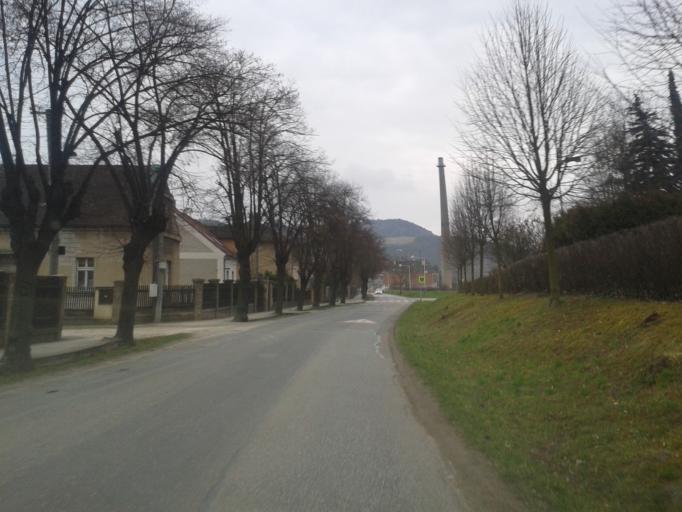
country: CZ
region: Central Bohemia
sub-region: Okres Beroun
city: Kraluv Dvur
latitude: 49.9484
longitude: 14.0307
